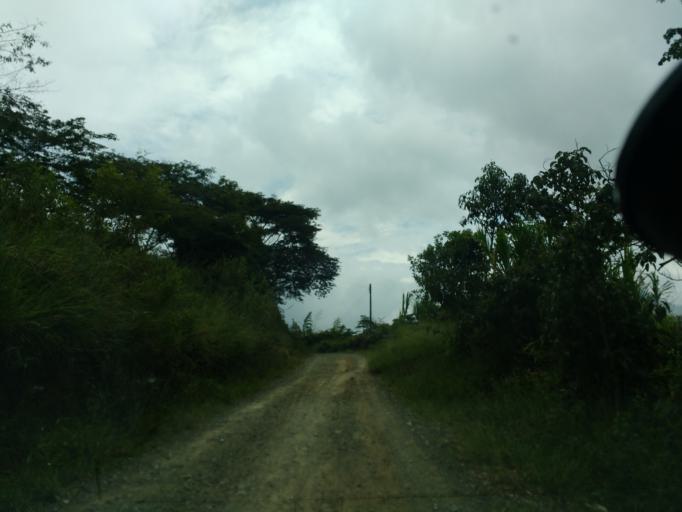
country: CO
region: Cauca
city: Santander de Quilichao
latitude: 2.9126
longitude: -76.4813
